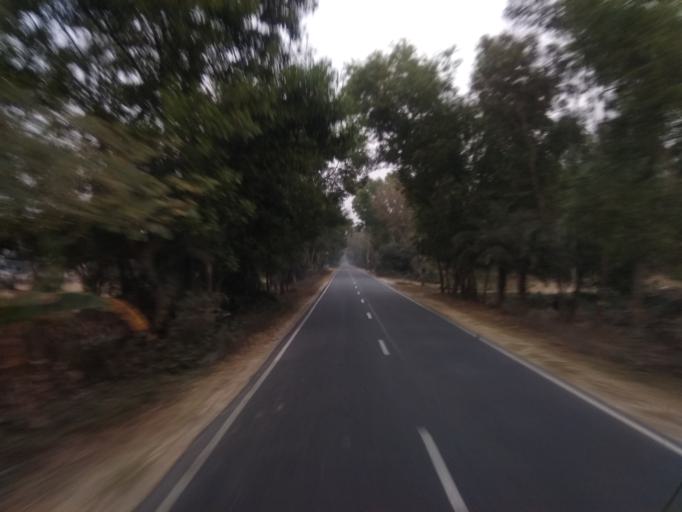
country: BD
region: Rajshahi
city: Bogra
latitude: 24.6541
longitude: 89.2614
